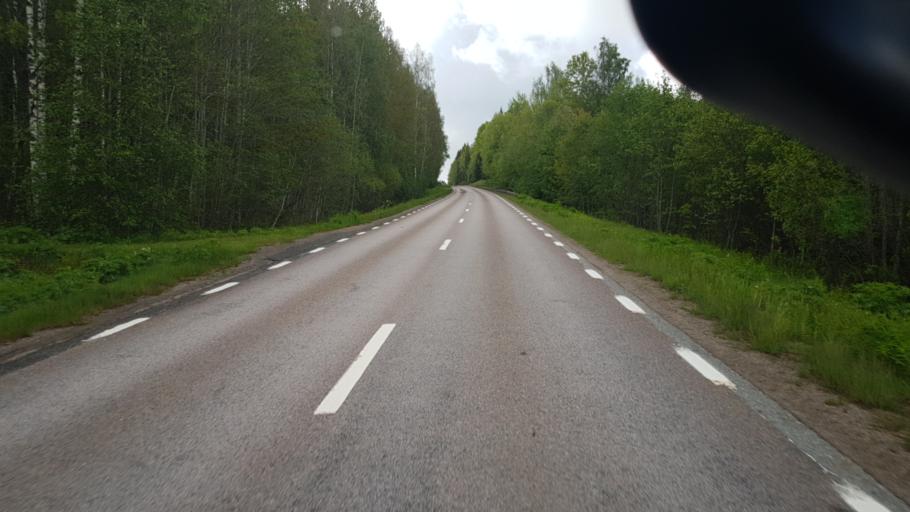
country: SE
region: Vaermland
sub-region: Eda Kommun
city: Amotfors
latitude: 59.7036
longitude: 12.3091
